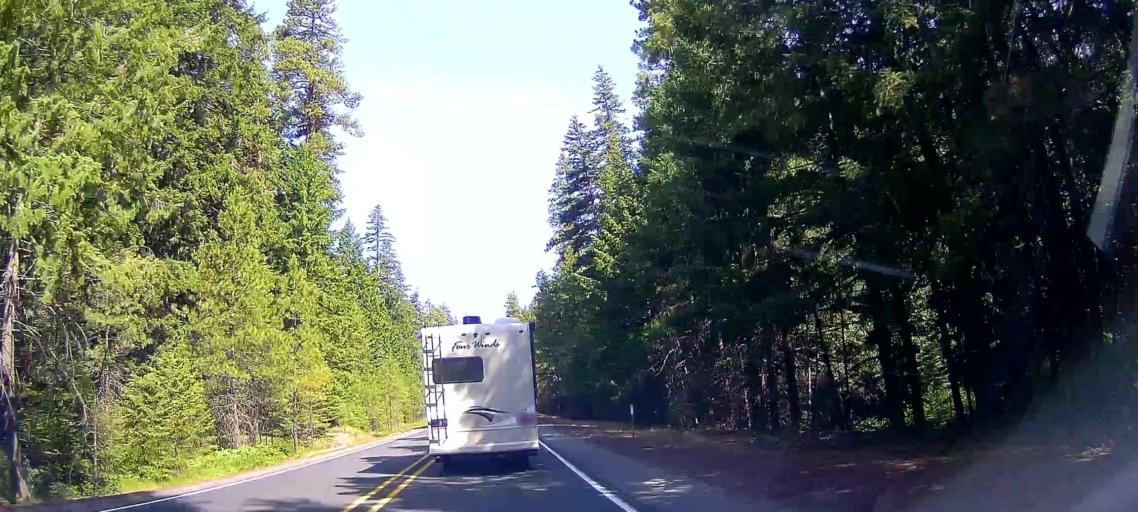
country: US
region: Oregon
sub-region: Jefferson County
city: Warm Springs
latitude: 45.0754
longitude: -121.5365
